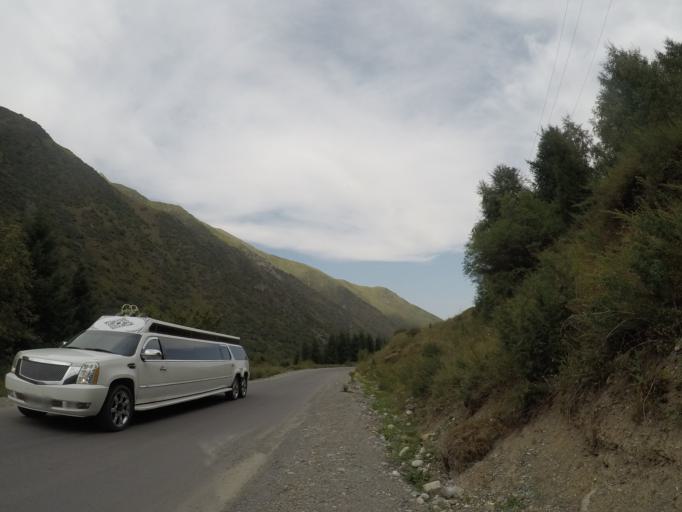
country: KG
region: Chuy
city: Bishkek
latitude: 42.5903
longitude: 74.4835
